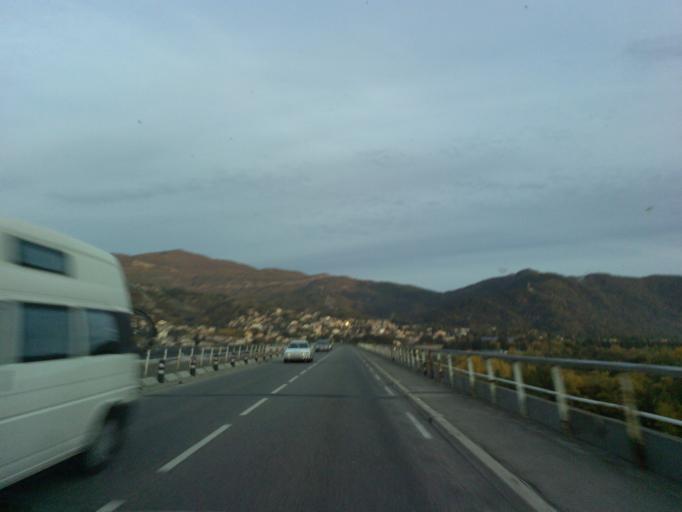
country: FR
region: Provence-Alpes-Cote d'Azur
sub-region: Departement des Alpes-de-Haute-Provence
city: Volonne
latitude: 44.0858
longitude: 6.0111
